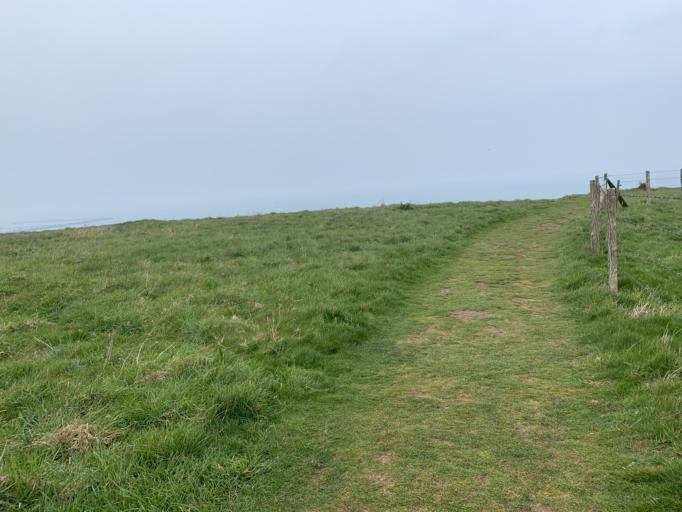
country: FR
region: Haute-Normandie
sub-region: Departement de la Seine-Maritime
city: Saint-Jouin-Bruneval
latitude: 49.6838
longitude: 0.1649
